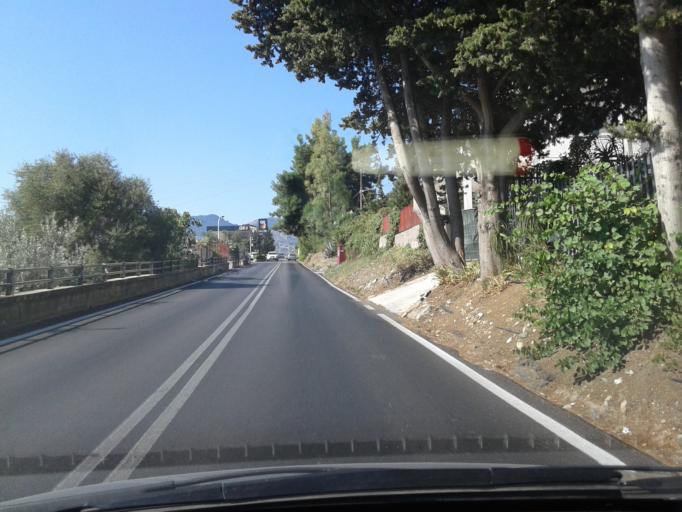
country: IT
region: Sicily
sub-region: Palermo
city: Cannizzaro-Favara
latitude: 38.0657
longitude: 13.2675
